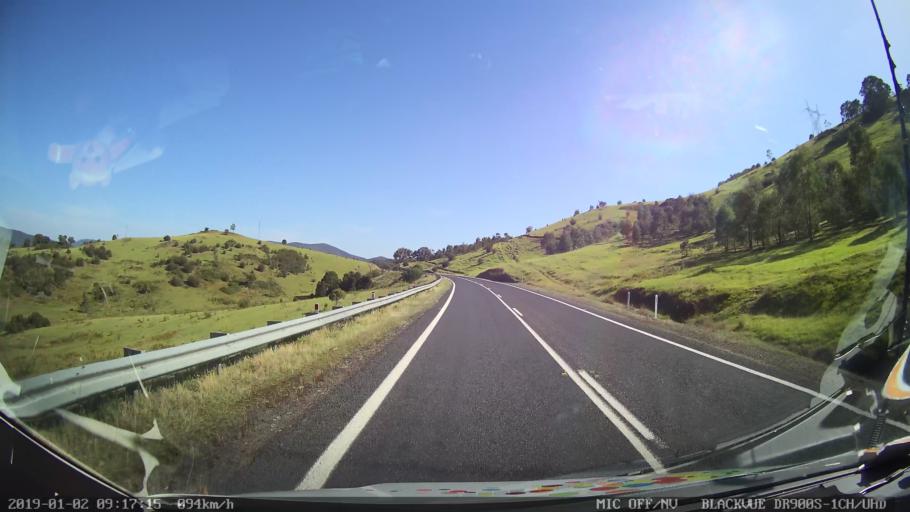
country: AU
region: New South Wales
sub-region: Tumut Shire
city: Tumut
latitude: -35.4434
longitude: 148.2869
